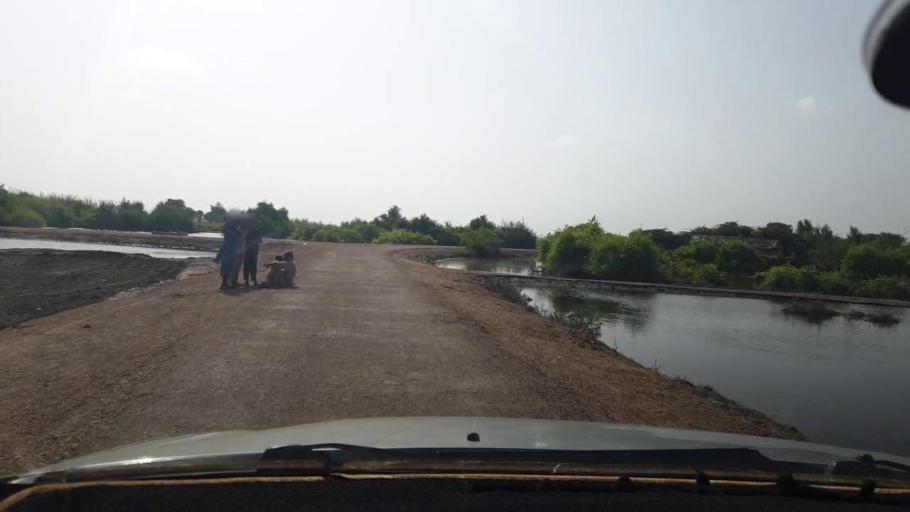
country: PK
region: Sindh
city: Tando Bago
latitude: 24.8076
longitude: 68.9159
